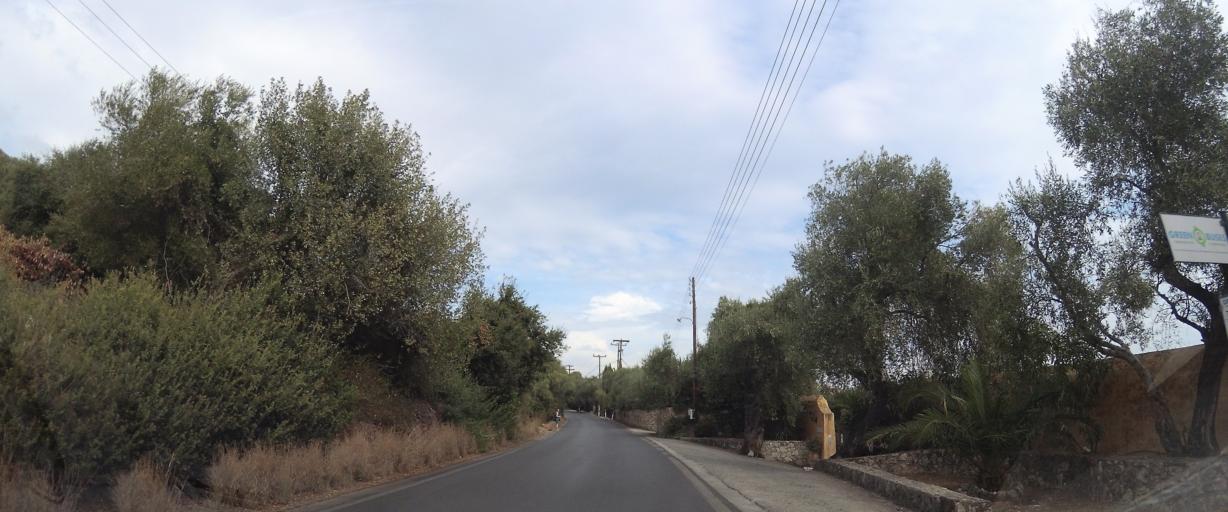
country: GR
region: Ionian Islands
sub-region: Nomos Kerkyras
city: Kontokali
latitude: 39.7098
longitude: 19.8566
